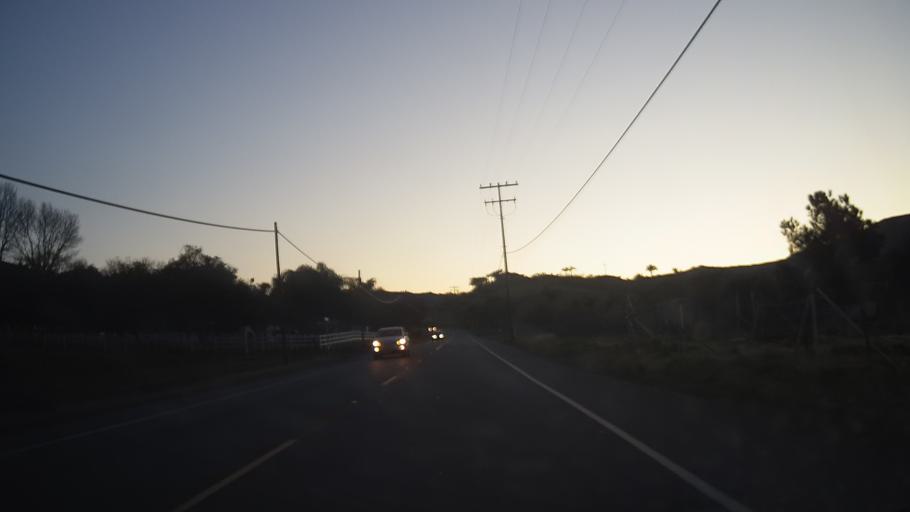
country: US
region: California
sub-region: San Diego County
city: Harbison Canyon
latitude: 32.7902
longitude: -116.8405
